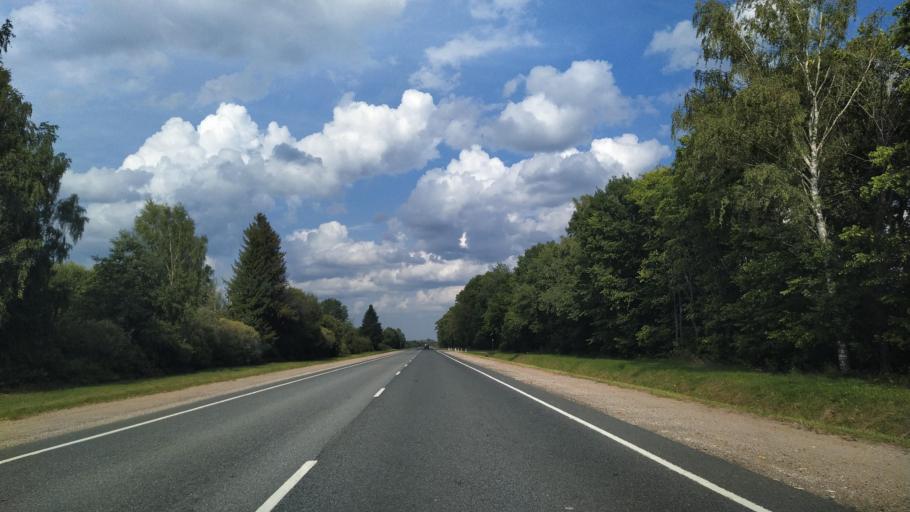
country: RU
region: Novgorod
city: Shimsk
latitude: 58.1911
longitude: 30.5657
